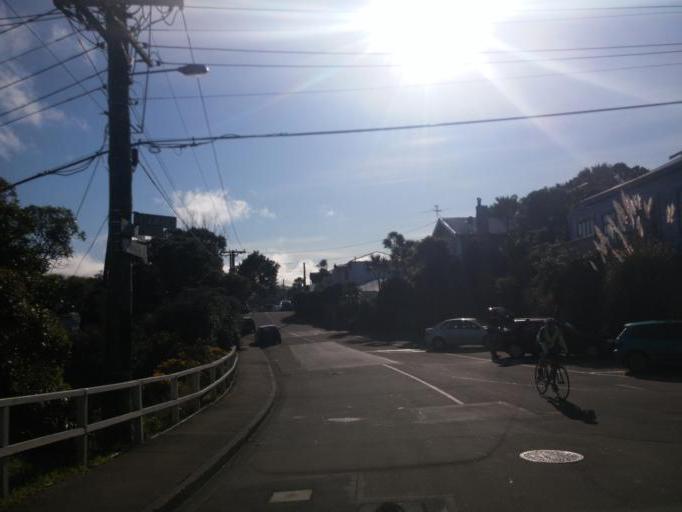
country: NZ
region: Wellington
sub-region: Wellington City
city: Brooklyn
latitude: -41.3088
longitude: 174.7644
